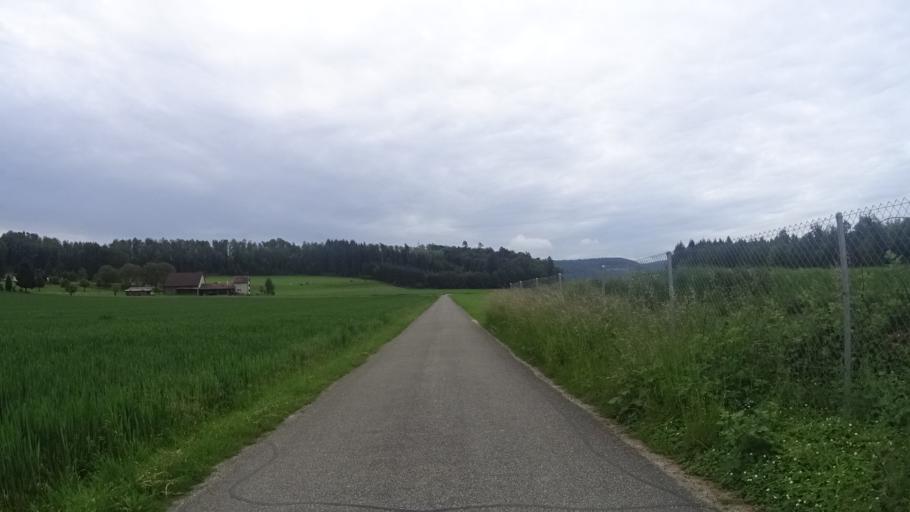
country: CH
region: Aargau
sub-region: Bezirk Baden
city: Wurenlingen
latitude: 47.5547
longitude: 8.2523
